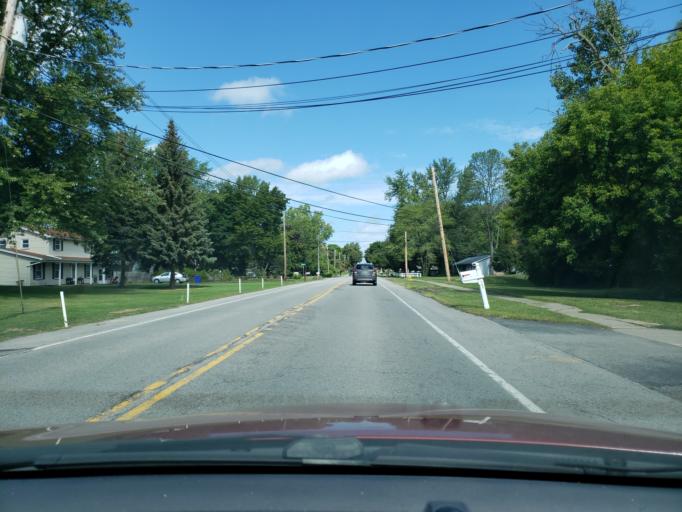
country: US
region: New York
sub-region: Monroe County
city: Greece
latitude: 43.2481
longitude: -77.7330
